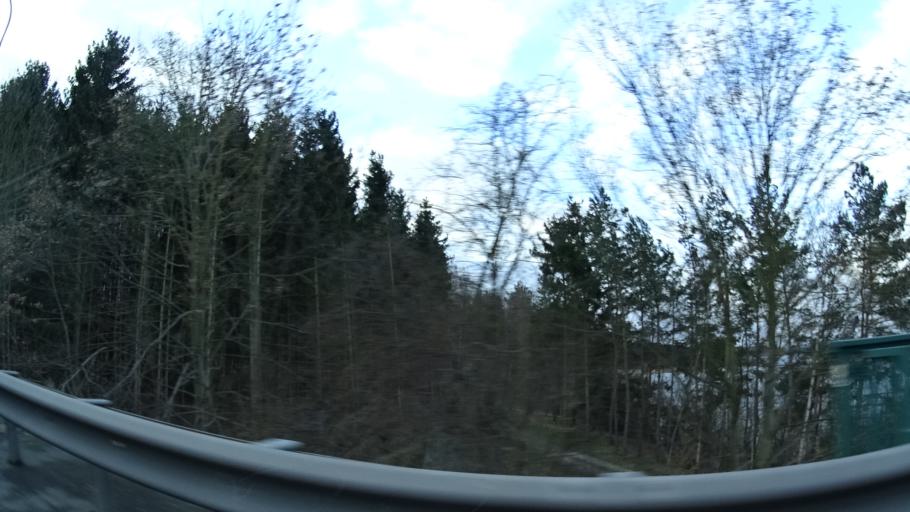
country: DE
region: Thuringia
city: Zeulenroda
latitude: 50.6628
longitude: 11.9756
